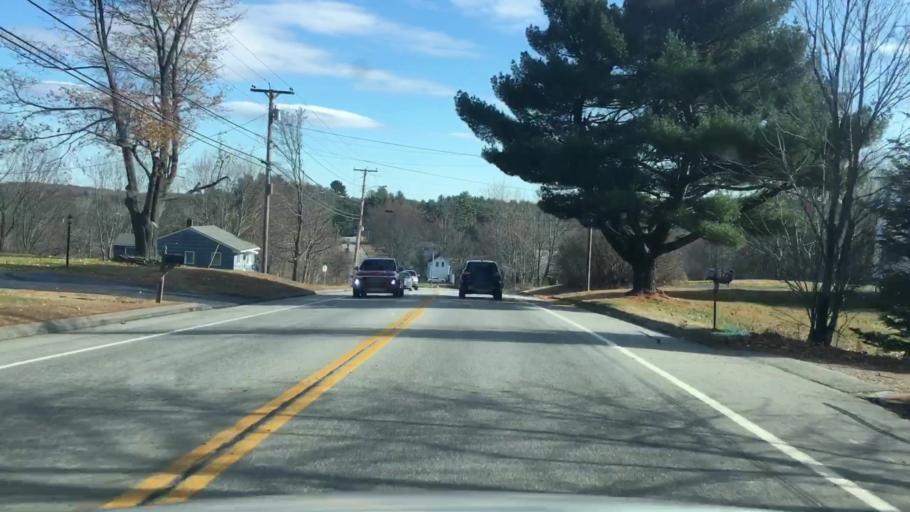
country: US
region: Maine
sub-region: Kennebec County
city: Chelsea
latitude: 44.2962
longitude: -69.7219
